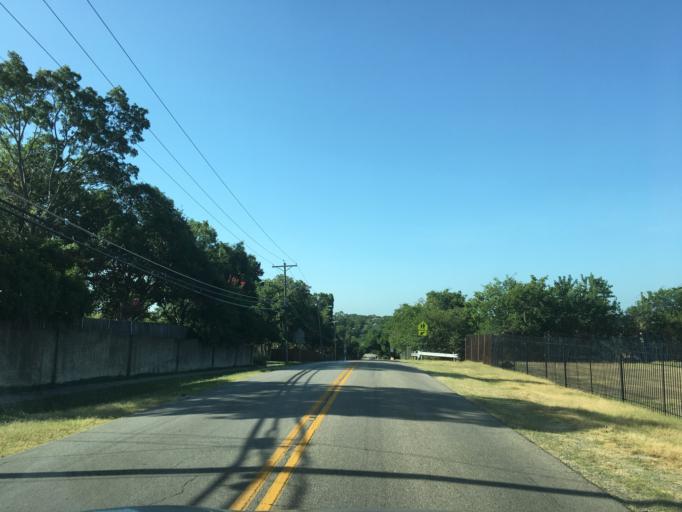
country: US
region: Texas
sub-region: Dallas County
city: Richardson
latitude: 32.8756
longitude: -96.7290
